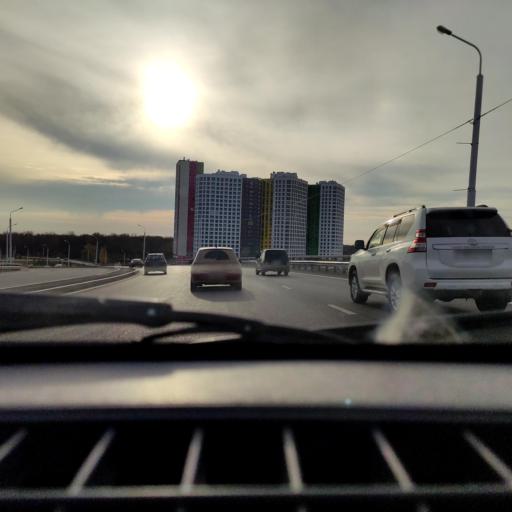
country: RU
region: Bashkortostan
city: Mikhaylovka
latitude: 54.7017
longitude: 55.8598
